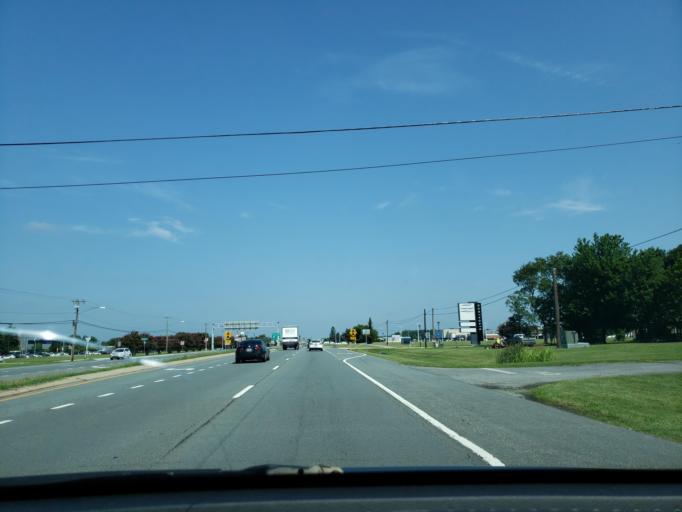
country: US
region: Delaware
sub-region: Kent County
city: Dover
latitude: 39.1471
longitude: -75.5013
